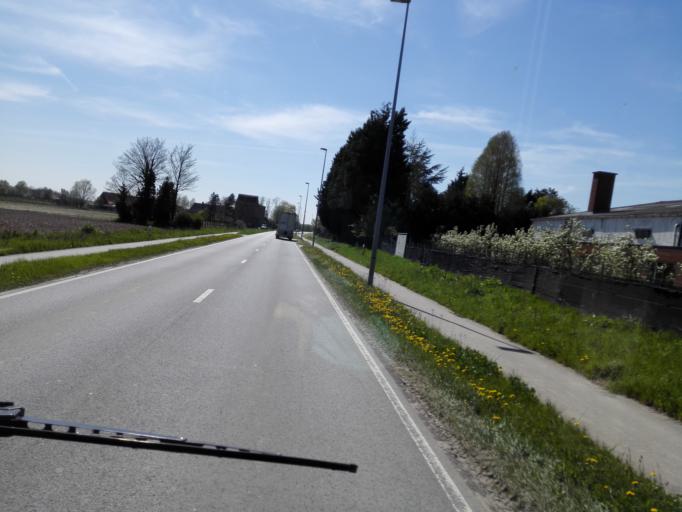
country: BE
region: Flanders
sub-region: Provincie West-Vlaanderen
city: Meulebeke
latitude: 50.9383
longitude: 3.2718
